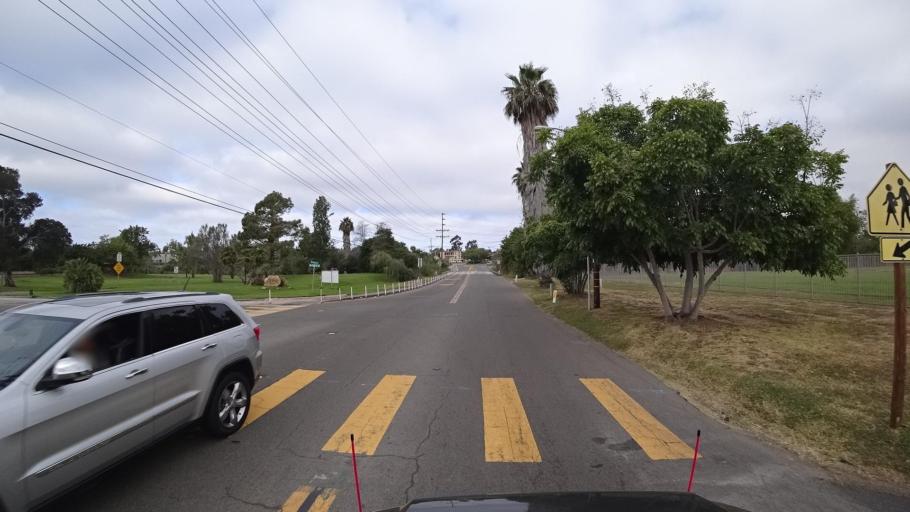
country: US
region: California
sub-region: San Diego County
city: Lake San Marcos
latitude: 33.1299
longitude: -117.1996
